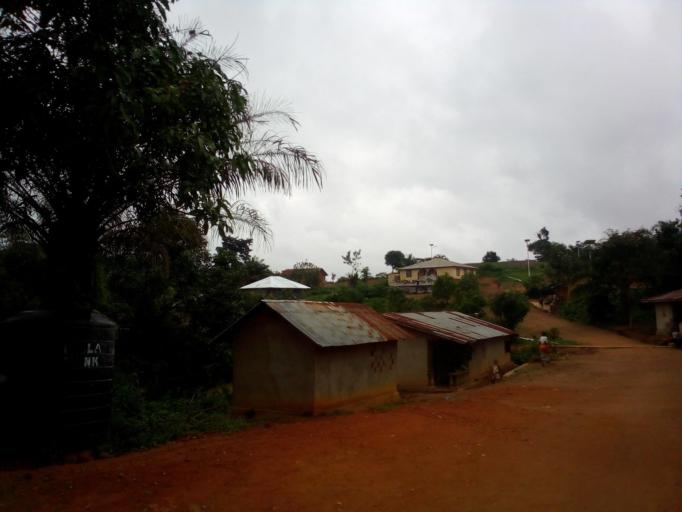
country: SL
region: Eastern Province
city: Kailahun
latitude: 8.2732
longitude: -10.5810
